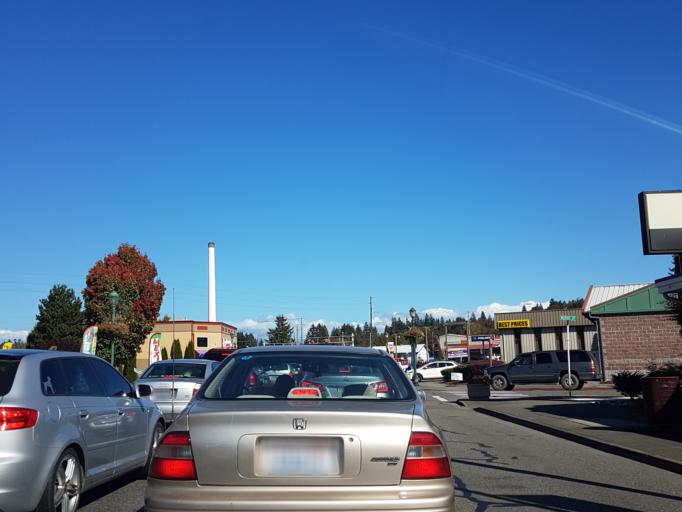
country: US
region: Washington
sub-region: Snohomish County
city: Monroe
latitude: 47.8564
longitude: -121.9686
